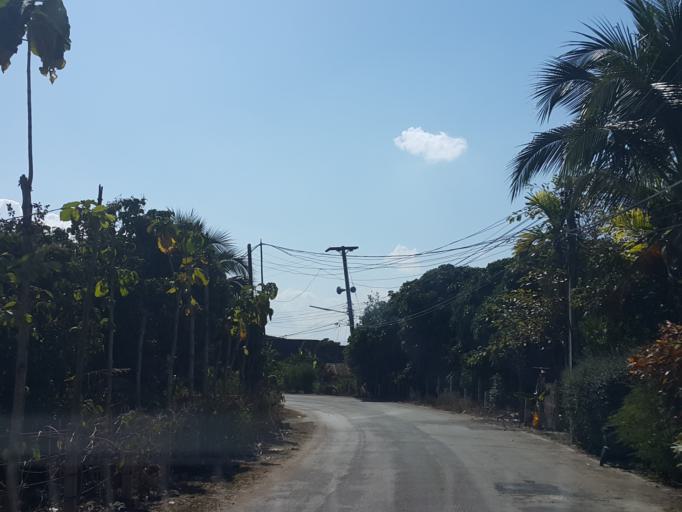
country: TH
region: Chiang Mai
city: Mae Taeng
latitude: 19.0964
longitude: 98.9444
